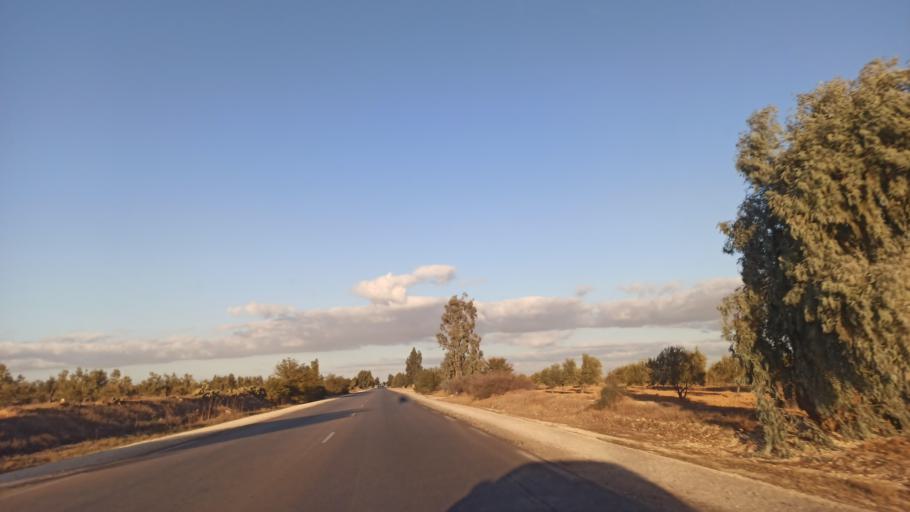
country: TN
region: Al Qayrawan
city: Sbikha
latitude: 35.8655
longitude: 10.2113
